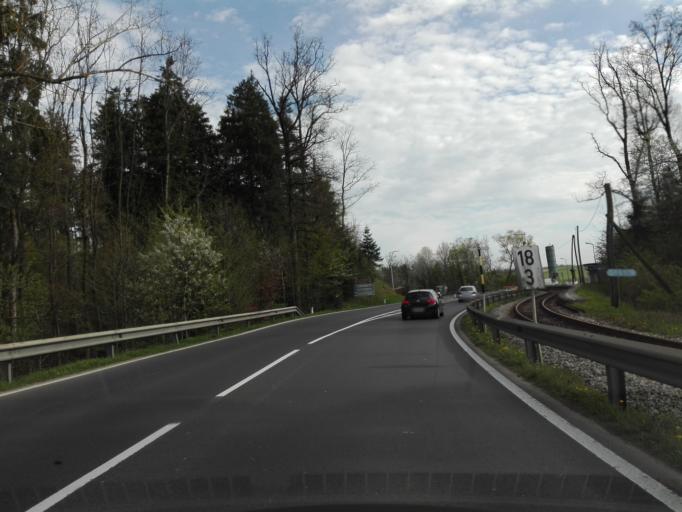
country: AT
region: Upper Austria
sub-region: Politischer Bezirk Urfahr-Umgebung
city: Sankt Gotthard im Muhlkreis
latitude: 48.3868
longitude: 14.0913
